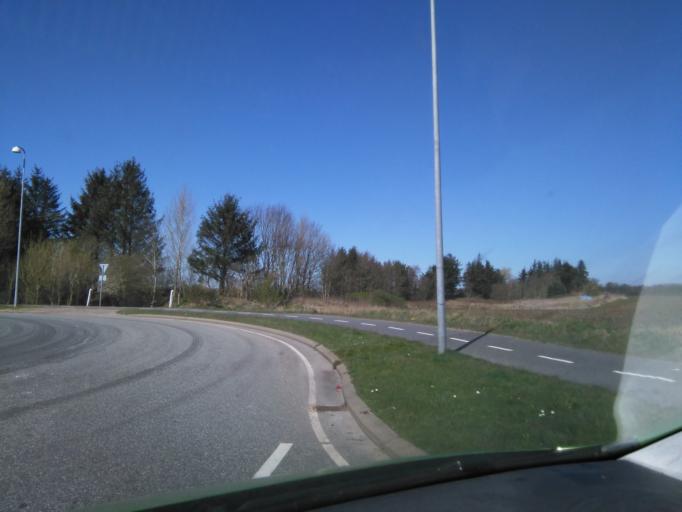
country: DK
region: South Denmark
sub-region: Varde Kommune
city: Oksbol
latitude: 55.6178
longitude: 8.3263
